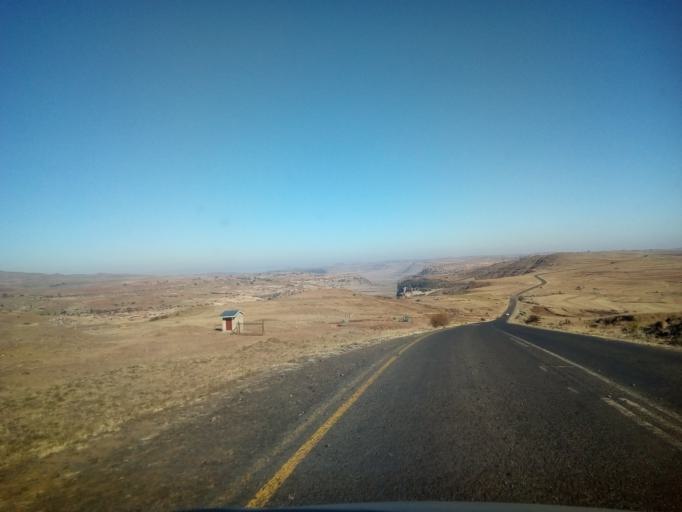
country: LS
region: Berea
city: Teyateyaneng
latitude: -29.2529
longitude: 27.7880
